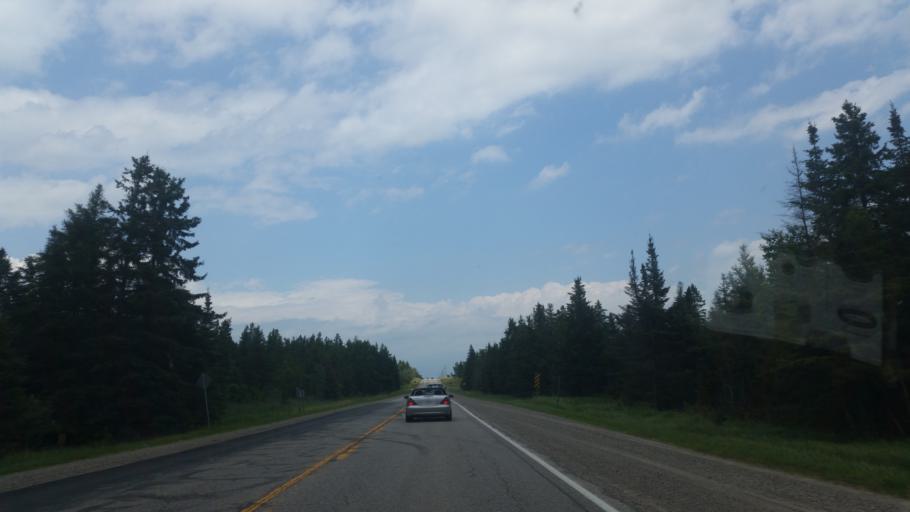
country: CA
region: Ontario
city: Orangeville
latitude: 43.7333
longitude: -80.0917
